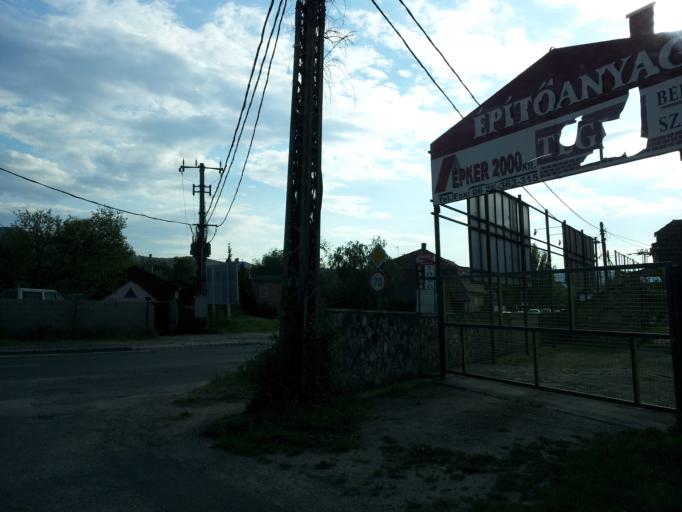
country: HU
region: Pest
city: Pilisborosjeno
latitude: 47.5966
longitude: 18.9777
